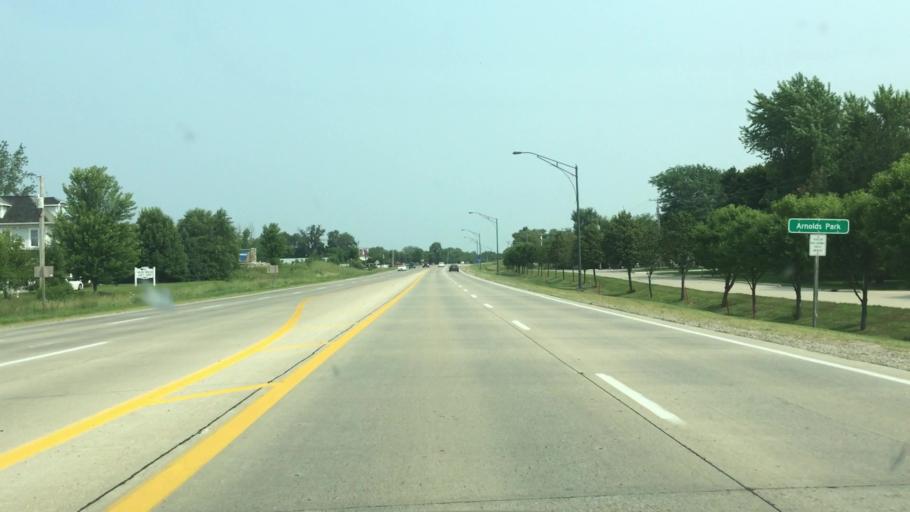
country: US
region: Iowa
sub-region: Dickinson County
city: Arnolds Park
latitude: 43.3539
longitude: -95.1421
